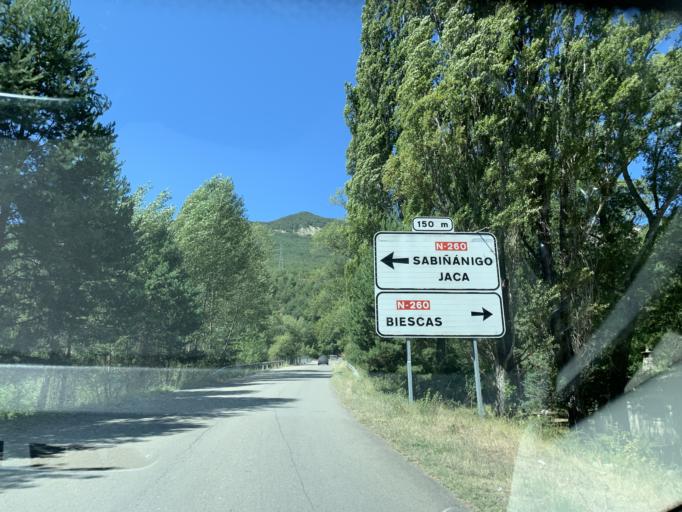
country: ES
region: Aragon
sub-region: Provincia de Huesca
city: Biescas
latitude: 42.5790
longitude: -0.3226
